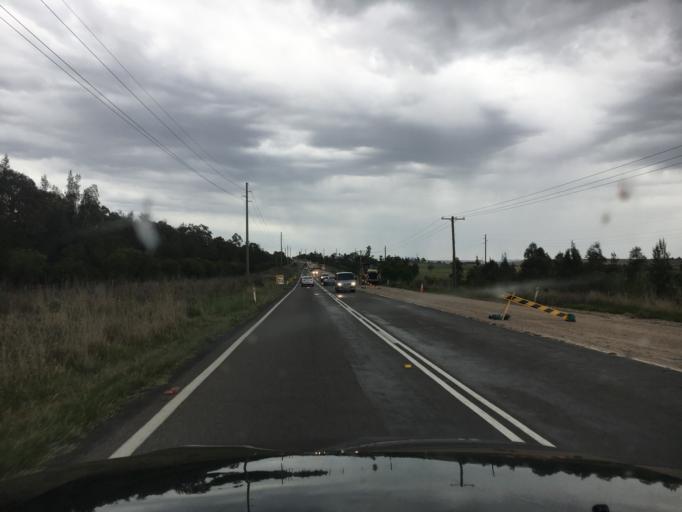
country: AU
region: New South Wales
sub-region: Muswellbrook
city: Muswellbrook
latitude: -32.1950
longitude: 150.8929
